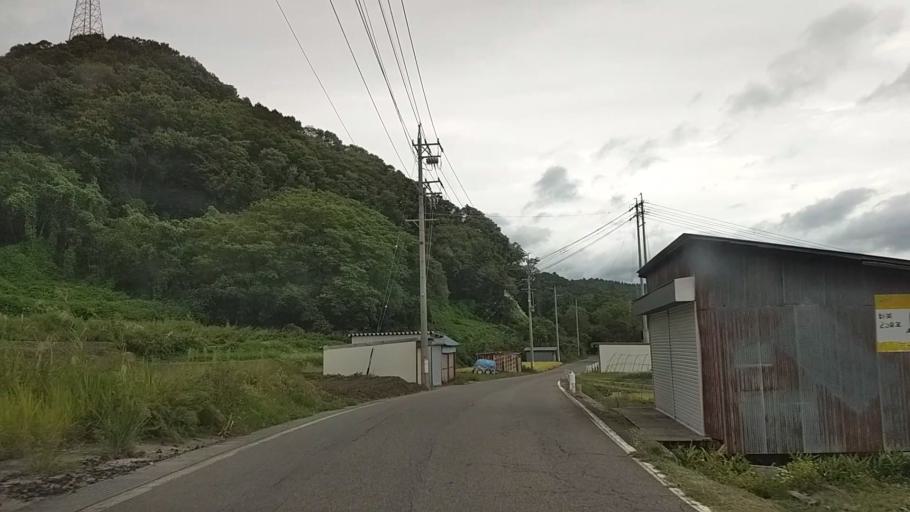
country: JP
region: Nagano
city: Nakano
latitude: 36.7977
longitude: 138.3439
